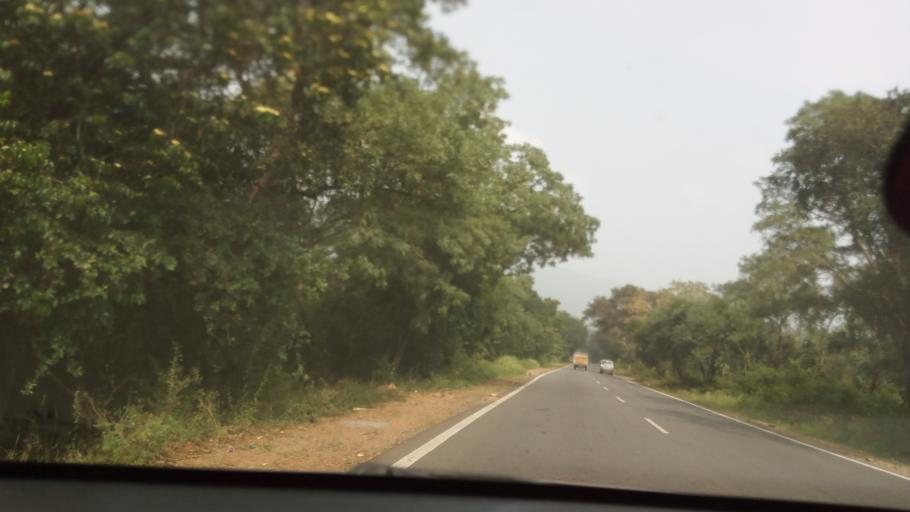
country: IN
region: Tamil Nadu
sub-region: Erode
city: Sathyamangalam
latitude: 11.5778
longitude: 77.1330
